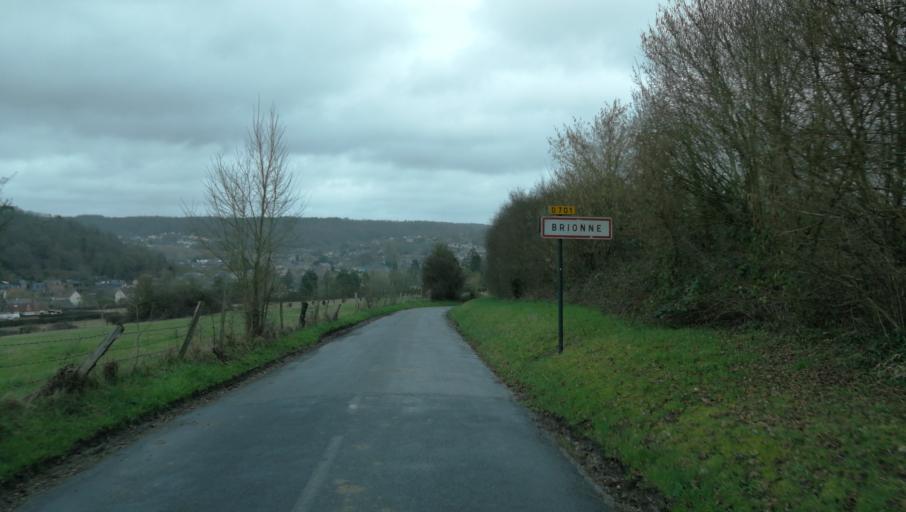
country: FR
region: Haute-Normandie
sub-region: Departement de l'Eure
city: Brionne
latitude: 49.1910
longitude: 0.7046
